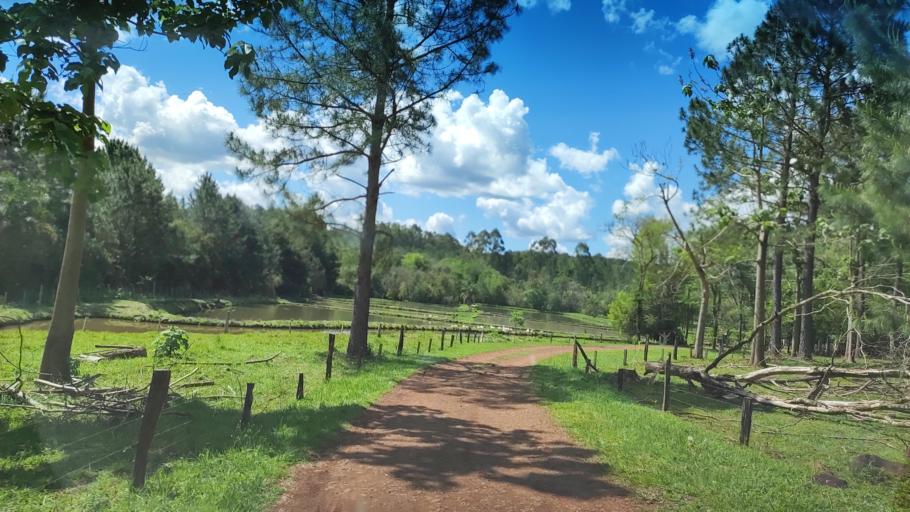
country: AR
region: Misiones
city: Ruiz de Montoya
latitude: -26.9510
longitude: -55.0082
